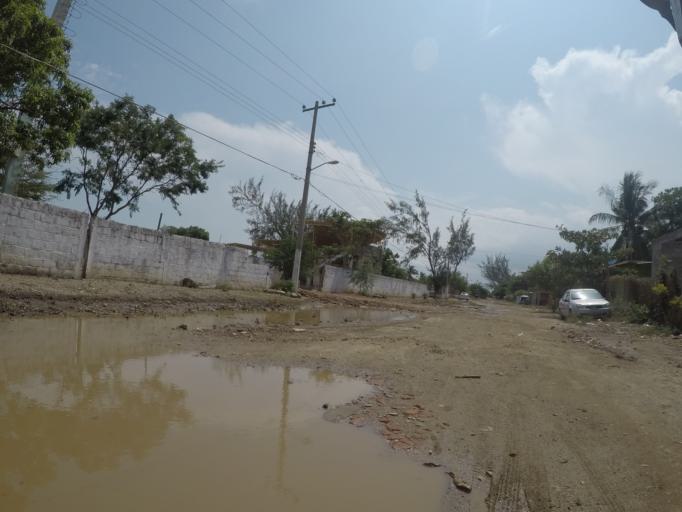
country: MX
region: Oaxaca
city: Union Hidalgo
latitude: 16.4655
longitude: -94.8299
